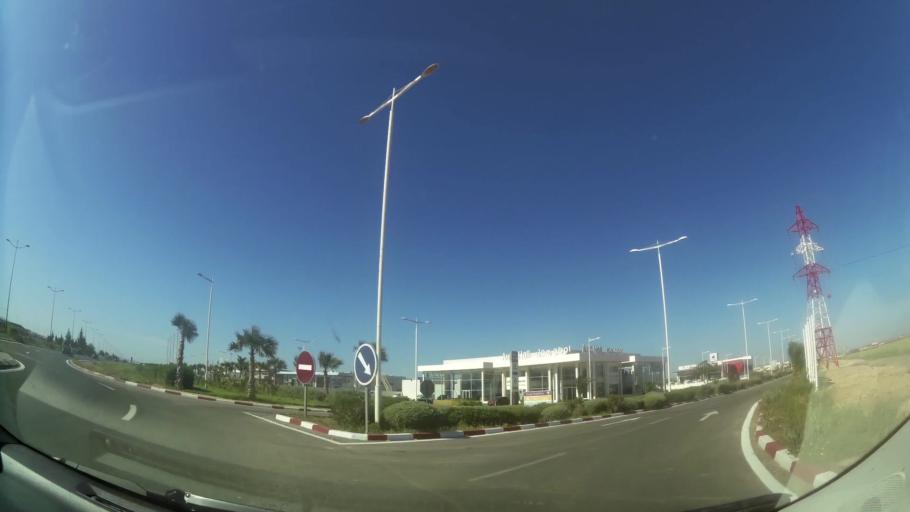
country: MA
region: Oriental
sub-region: Oujda-Angad
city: Oujda
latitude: 34.7667
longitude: -1.9404
